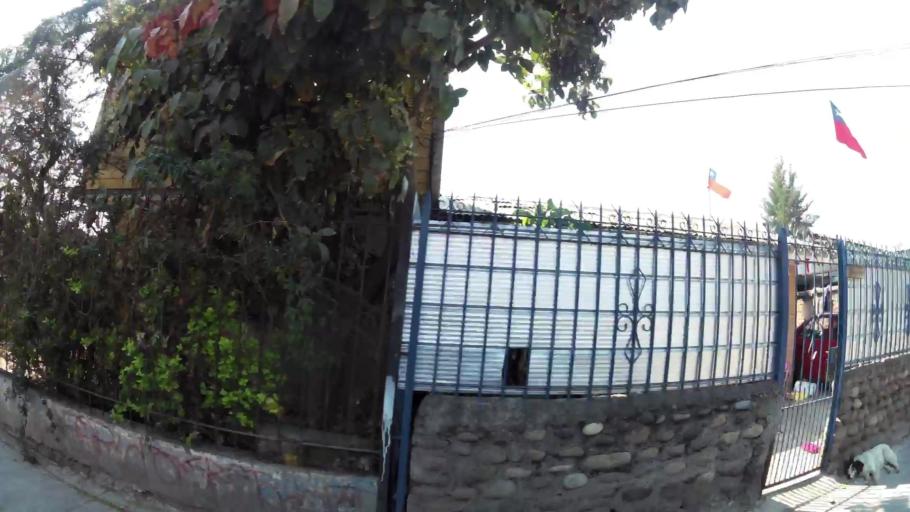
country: CL
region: Santiago Metropolitan
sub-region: Provincia de Santiago
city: La Pintana
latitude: -33.5435
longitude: -70.6029
